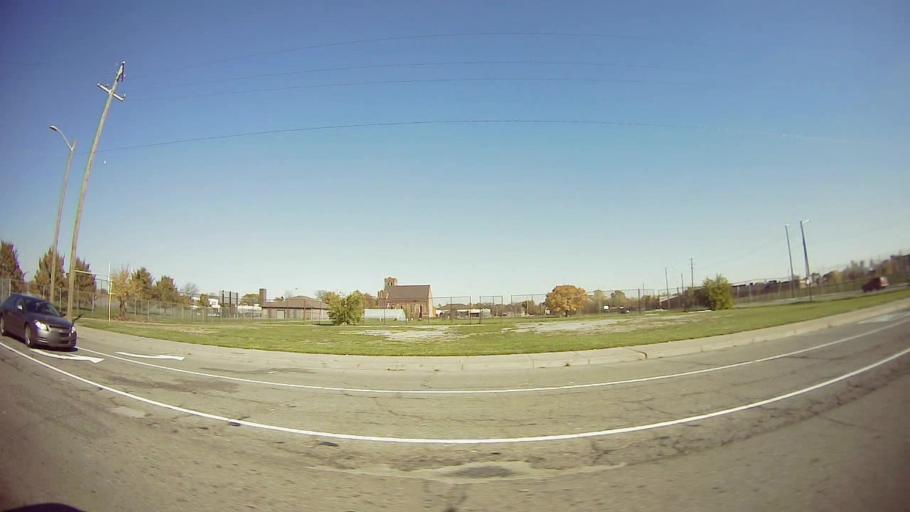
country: US
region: Michigan
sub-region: Wayne County
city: Detroit
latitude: 42.3477
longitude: -83.0859
